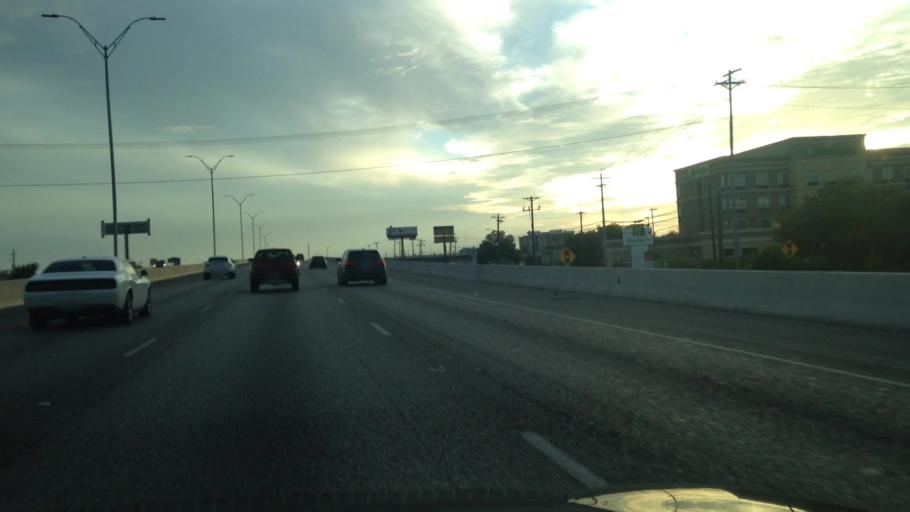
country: US
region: Texas
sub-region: Hays County
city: San Marcos
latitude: 29.8601
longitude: -97.9496
